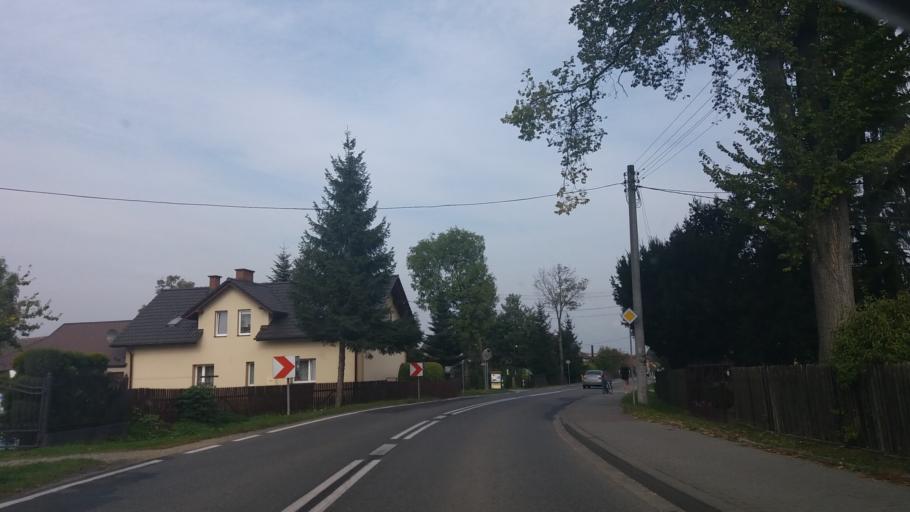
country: PL
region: Lesser Poland Voivodeship
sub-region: Powiat oswiecimski
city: Zator
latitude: 50.0181
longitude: 19.4330
